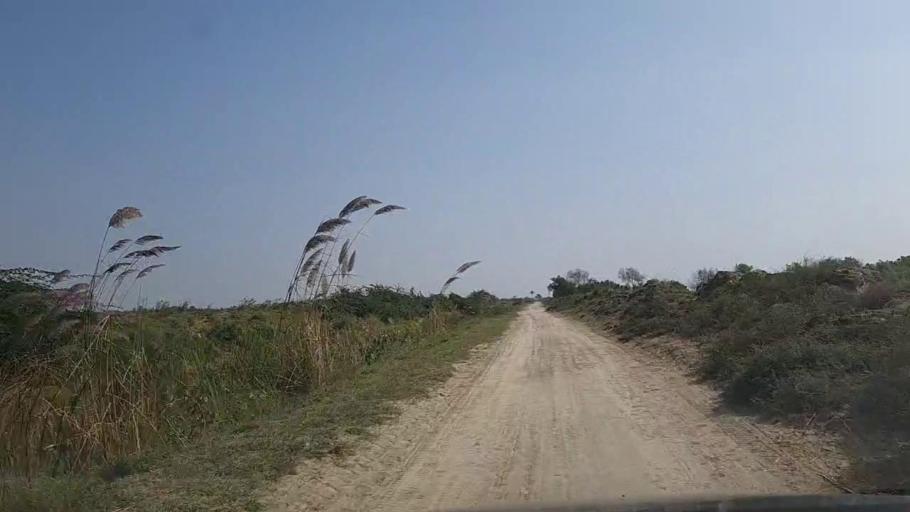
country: PK
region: Sindh
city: Gharo
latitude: 24.7155
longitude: 67.5716
